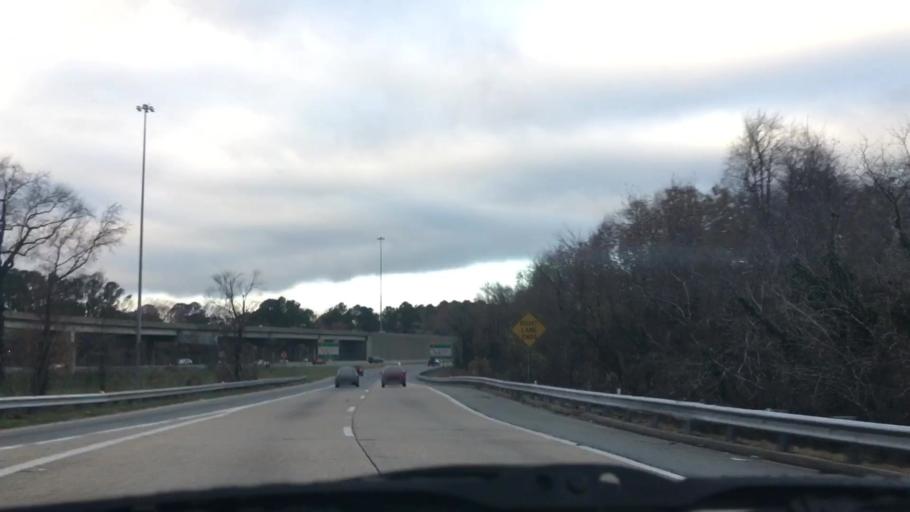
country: US
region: Virginia
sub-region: City of Chesapeake
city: Chesapeake
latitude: 36.8470
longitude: -76.1946
